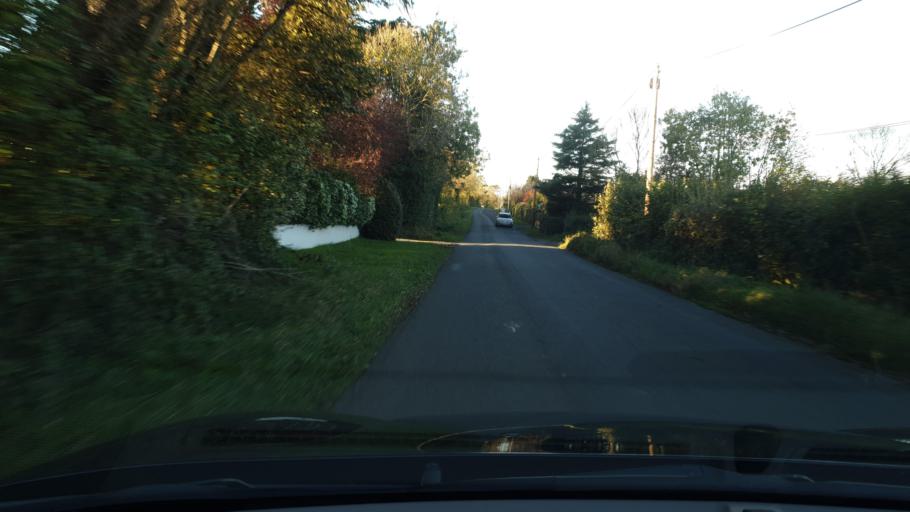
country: IE
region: Leinster
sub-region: Lu
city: Drogheda
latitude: 53.6813
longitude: -6.3305
